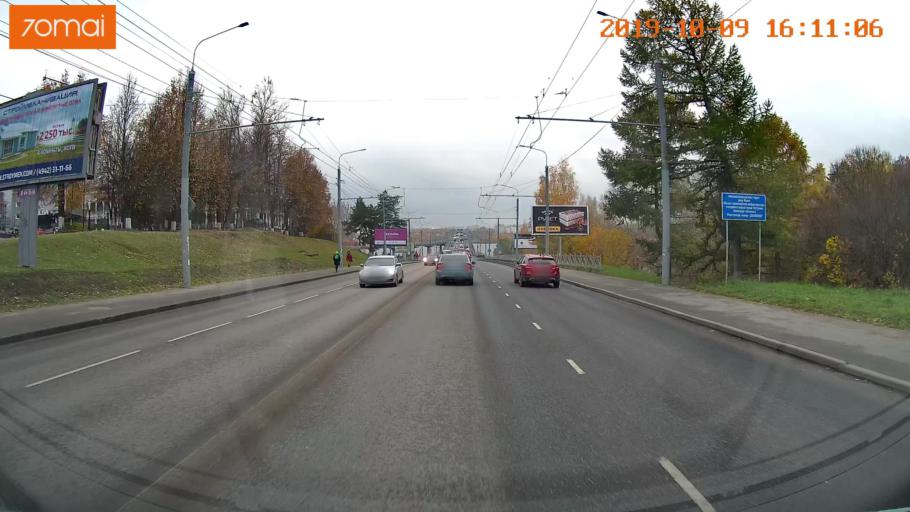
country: RU
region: Kostroma
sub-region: Kostromskoy Rayon
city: Kostroma
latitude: 57.7589
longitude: 40.9482
